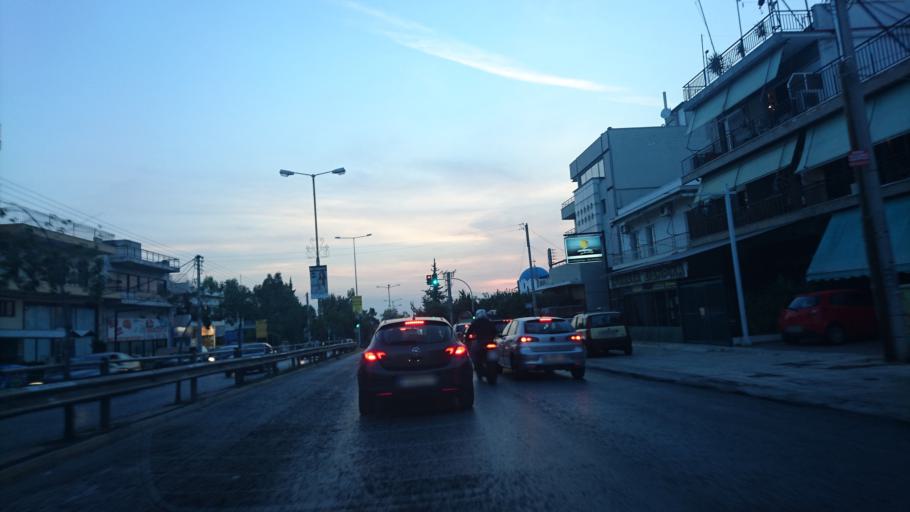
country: GR
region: Attica
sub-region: Nomarchia Athinas
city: Argyroupoli
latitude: 37.9105
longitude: 23.7418
